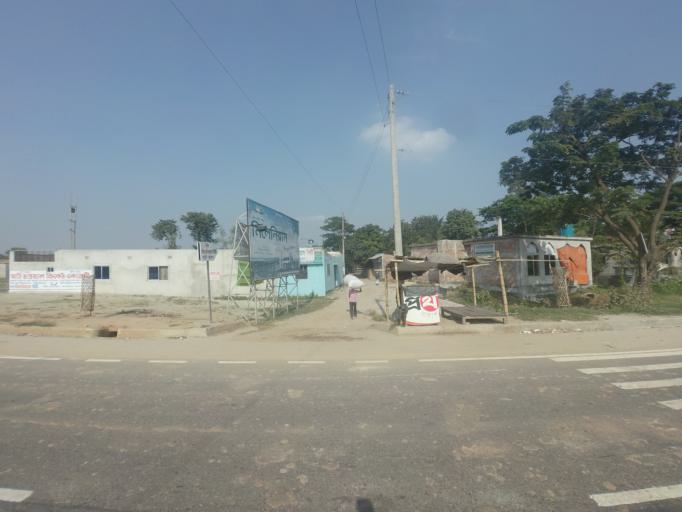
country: BD
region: Dhaka
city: Azimpur
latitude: 23.7352
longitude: 90.3295
